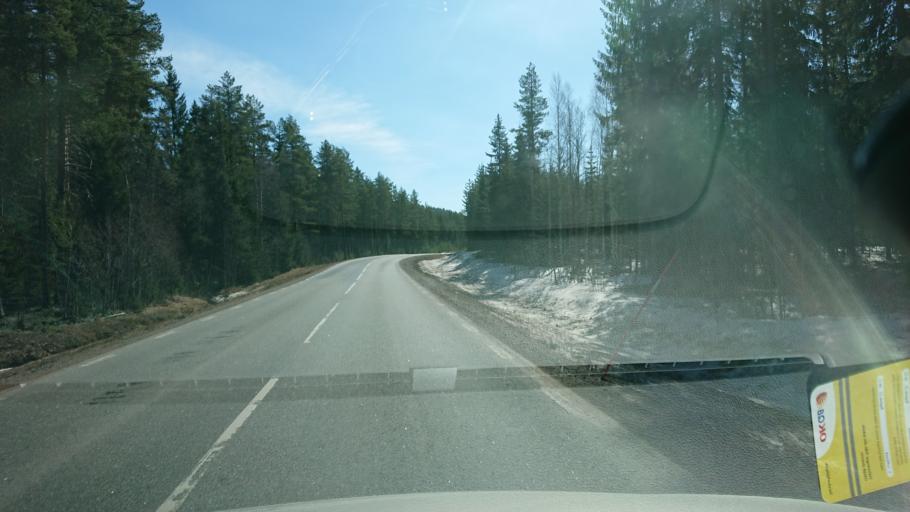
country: SE
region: Vaesternorrland
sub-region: Solleftea Kommun
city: As
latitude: 63.5693
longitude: 16.4522
